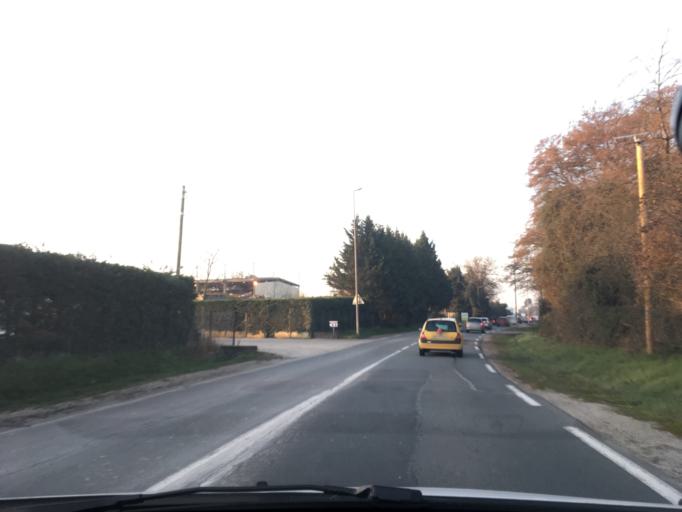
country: FR
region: Aquitaine
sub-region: Departement de la Gironde
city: Canejan
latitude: 44.7861
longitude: -0.6483
